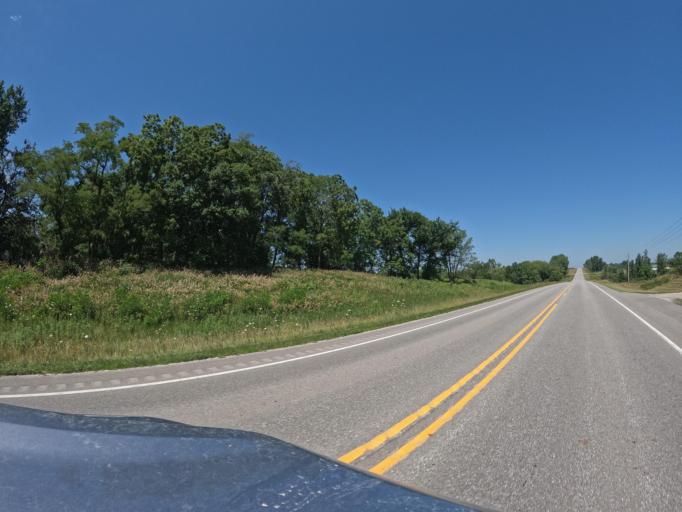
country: US
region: Iowa
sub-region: Keokuk County
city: Sigourney
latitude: 41.4630
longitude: -92.3551
